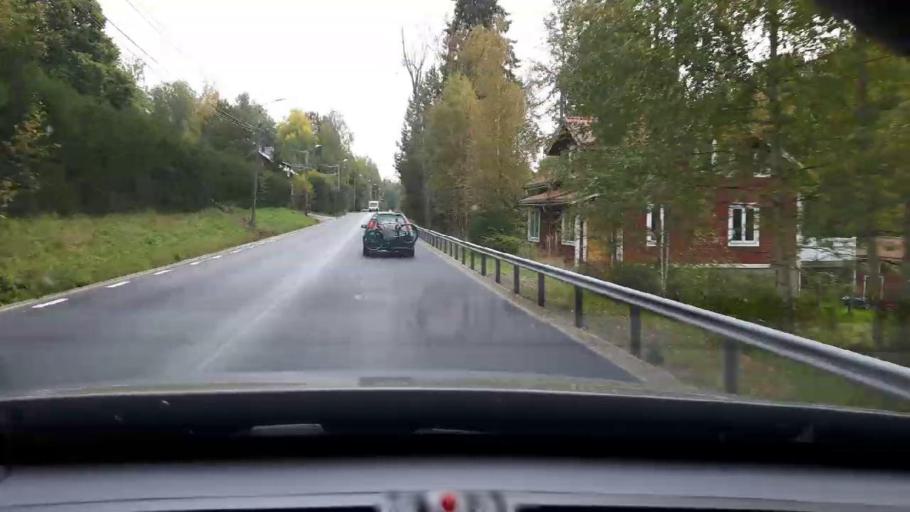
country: SE
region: Dalarna
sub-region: Ludvika Kommun
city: Ludvika
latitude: 60.1983
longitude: 15.1345
